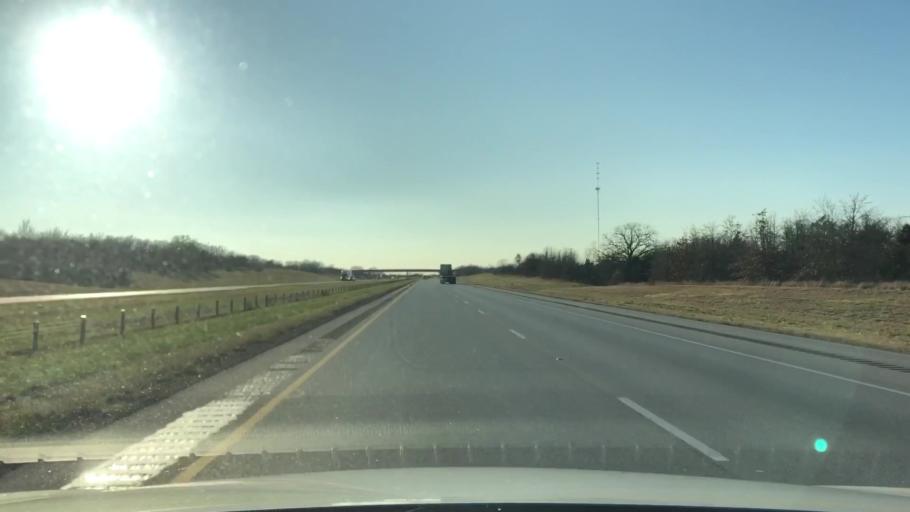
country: US
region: Texas
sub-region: Fayette County
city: Flatonia
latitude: 29.6956
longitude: -97.1508
